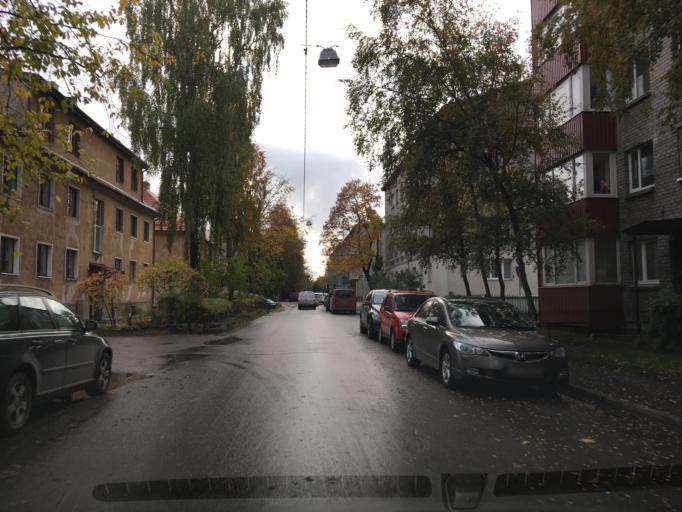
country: EE
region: Harju
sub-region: Tallinna linn
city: Tallinn
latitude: 59.4283
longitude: 24.7942
